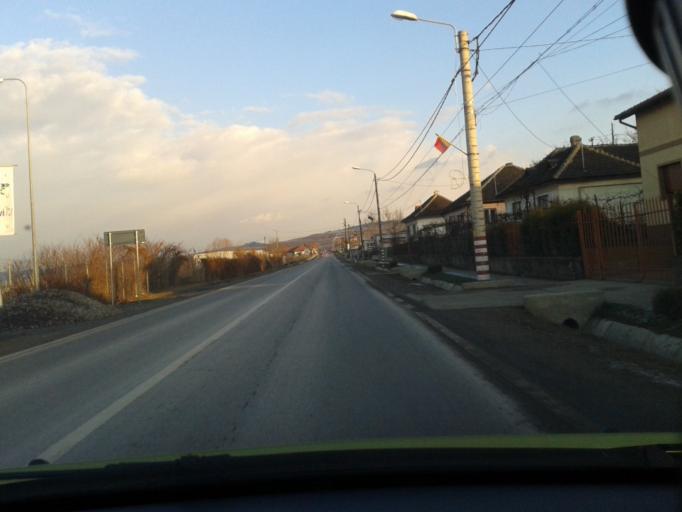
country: RO
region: Sibiu
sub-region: Comuna Copsa Mica
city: Copsa Mica
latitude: 46.1141
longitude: 24.2342
